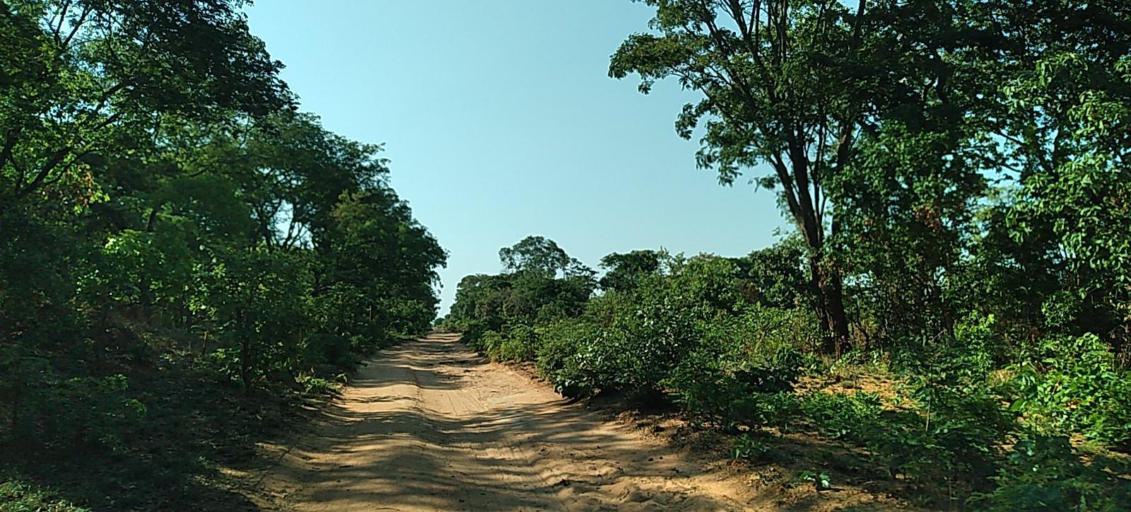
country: ZM
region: Central
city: Mkushi
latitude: -13.4609
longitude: 28.9118
